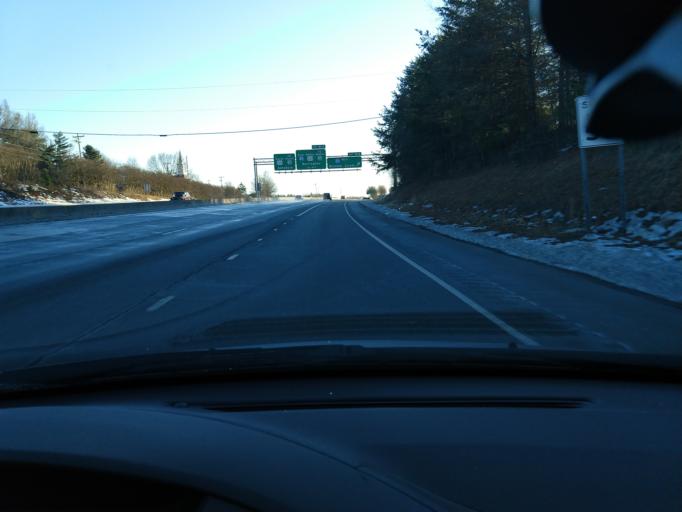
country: US
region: North Carolina
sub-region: Guilford County
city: Greensboro
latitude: 36.0395
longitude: -79.8183
